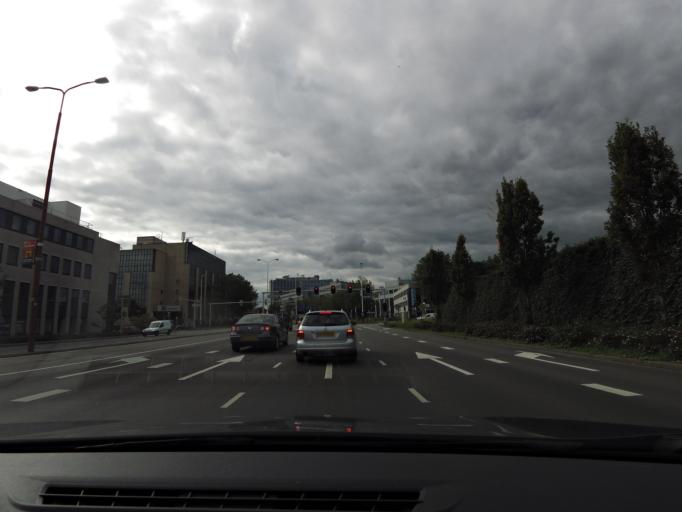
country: NL
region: Utrecht
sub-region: Gemeente Nieuwegein
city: Nieuwegein
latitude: 52.0279
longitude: 5.0700
